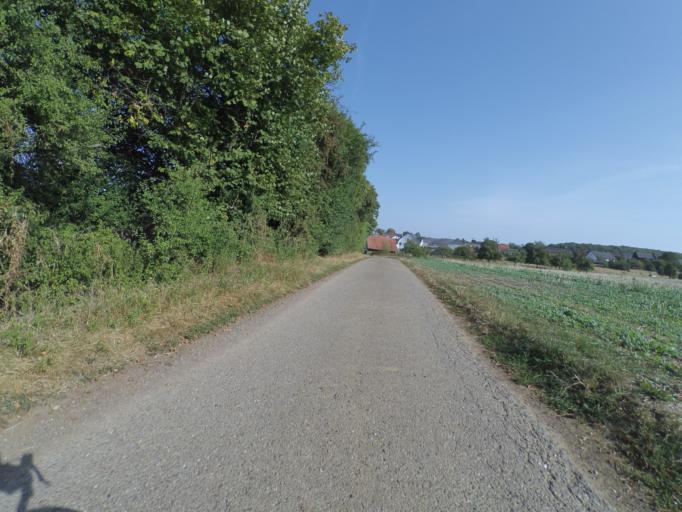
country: DE
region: Rheinland-Pfalz
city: Kirf
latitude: 49.5541
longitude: 6.4473
